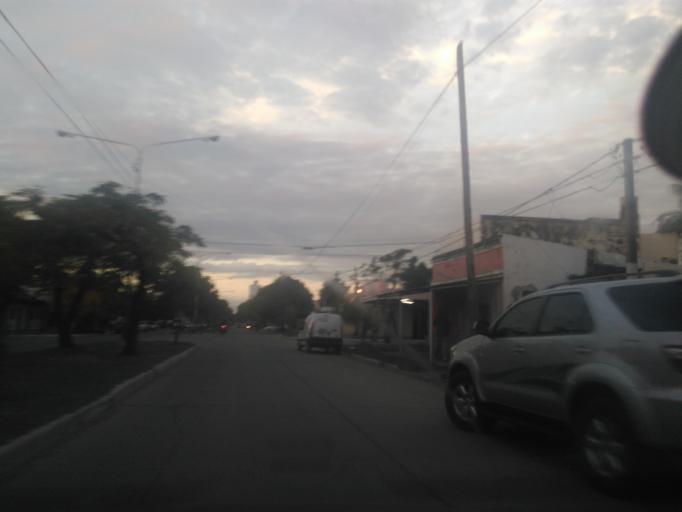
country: AR
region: Chaco
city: Resistencia
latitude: -27.4659
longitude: -58.9941
